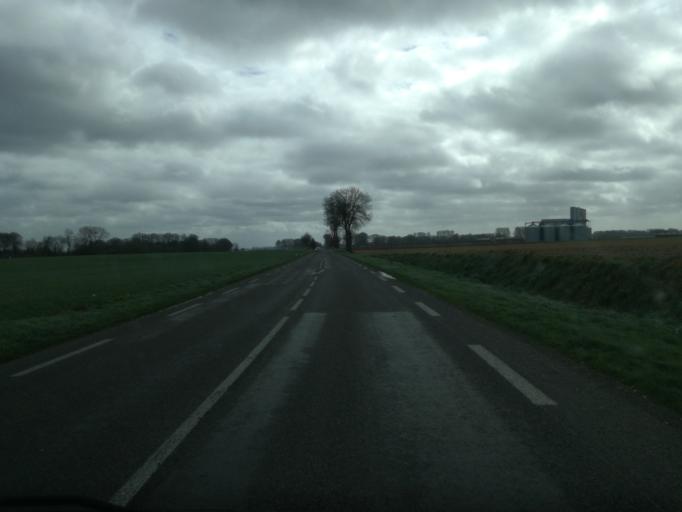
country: FR
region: Haute-Normandie
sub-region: Departement de la Seine-Maritime
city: Valliquerville
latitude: 49.6268
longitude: 0.6436
